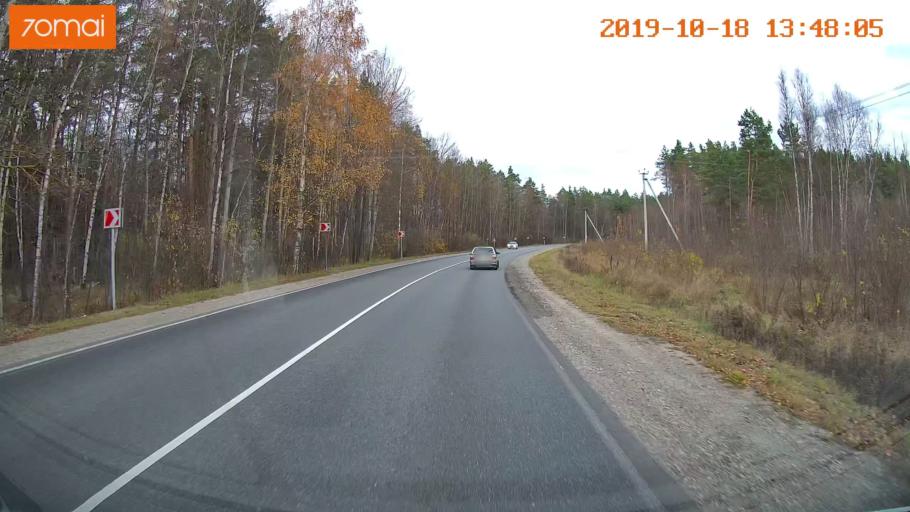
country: RU
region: Moskovskaya
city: Radovitskiy
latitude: 54.9847
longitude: 39.9515
